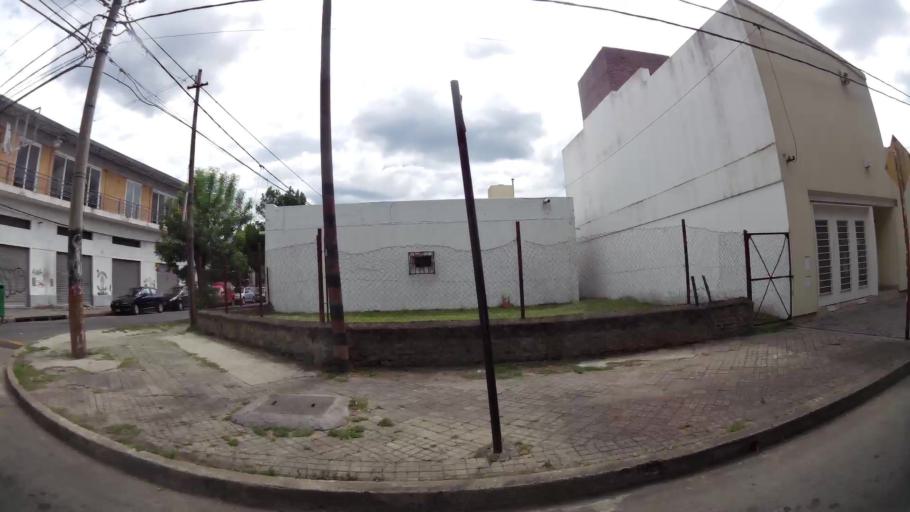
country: AR
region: Santa Fe
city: Gobernador Galvez
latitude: -32.9982
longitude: -60.6320
